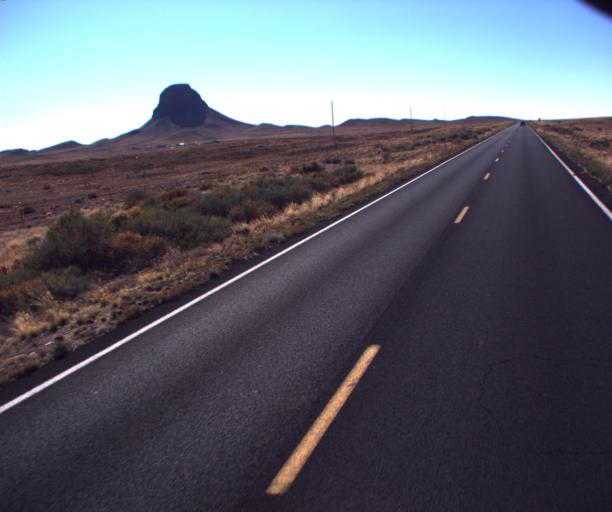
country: US
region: Arizona
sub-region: Navajo County
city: Dilkon
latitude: 35.3178
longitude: -110.4230
